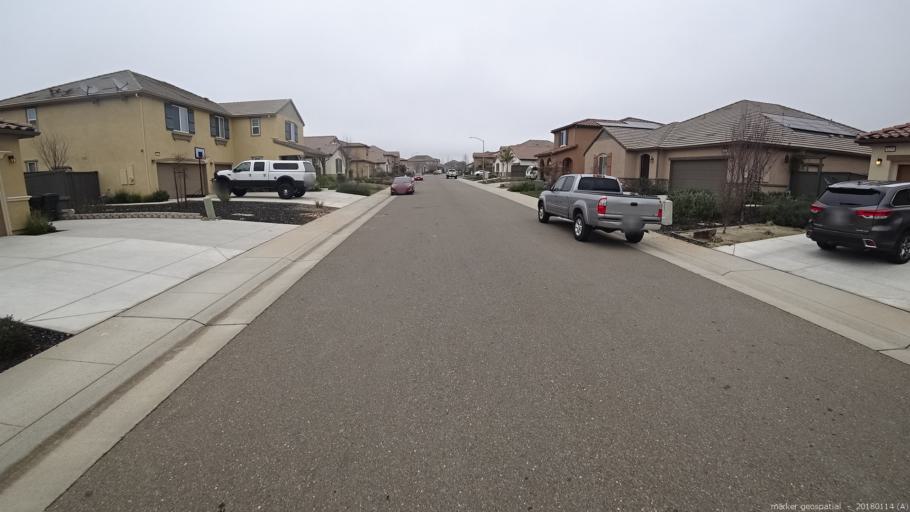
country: US
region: California
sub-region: Sacramento County
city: Rancho Cordova
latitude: 38.5287
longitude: -121.2317
